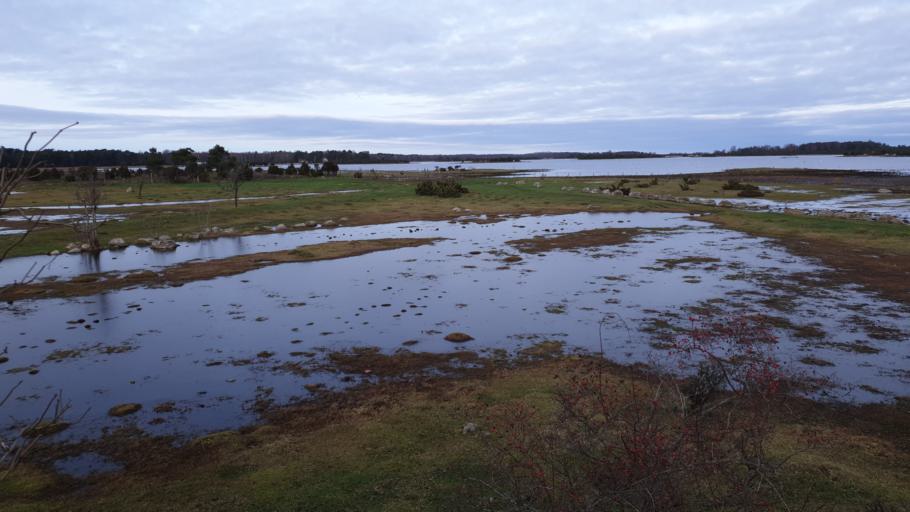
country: SE
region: Kalmar
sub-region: Torsas Kommun
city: Torsas
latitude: 56.2608
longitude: 16.0410
